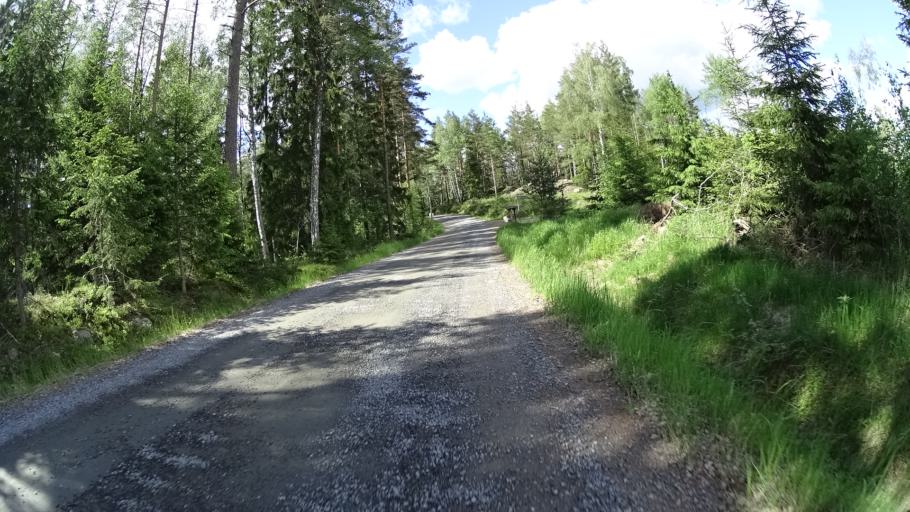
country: FI
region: Uusimaa
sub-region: Raaseporin
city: Pohja
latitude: 60.1806
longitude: 23.5864
